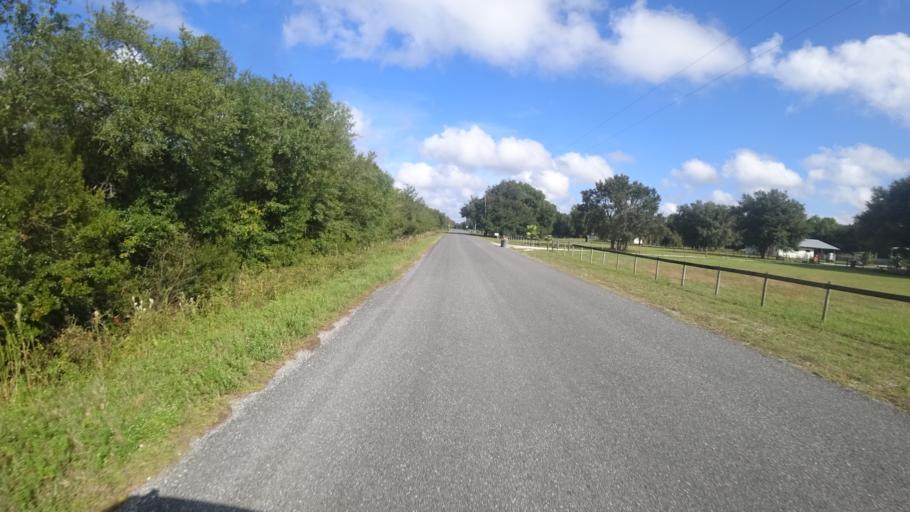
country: US
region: Florida
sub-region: Hillsborough County
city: Wimauma
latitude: 27.4659
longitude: -82.1532
